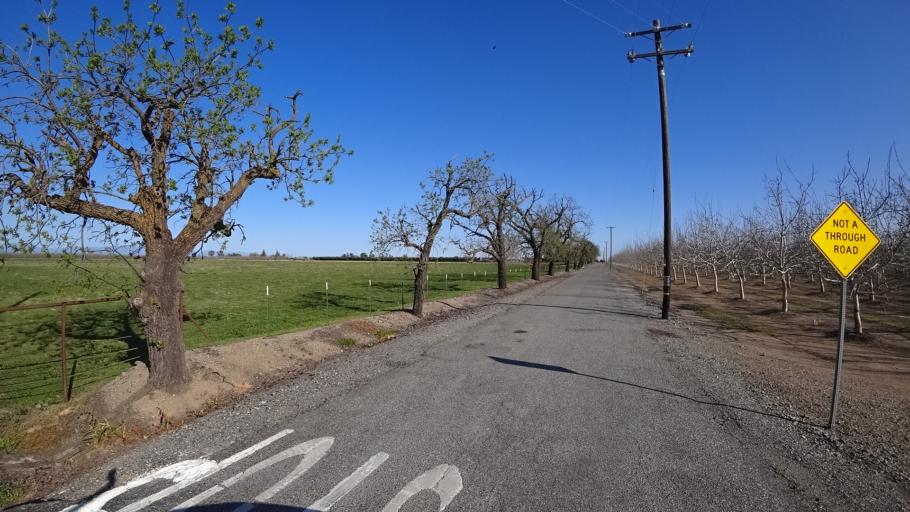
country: US
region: California
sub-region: Glenn County
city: Orland
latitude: 39.7574
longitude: -122.1134
